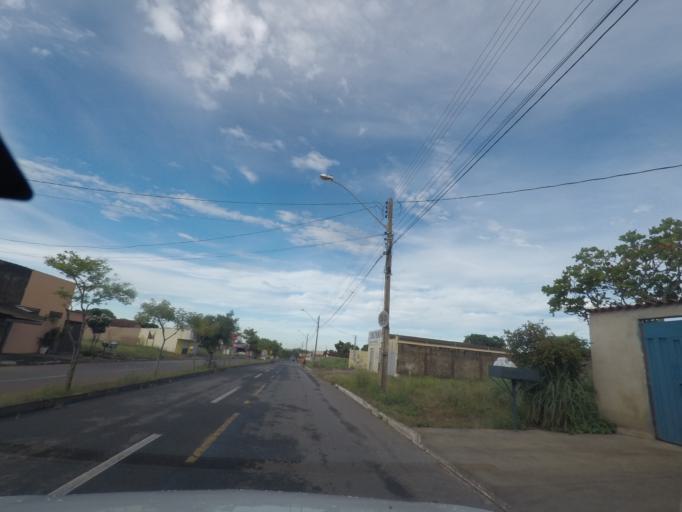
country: BR
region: Goias
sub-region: Aparecida De Goiania
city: Aparecida de Goiania
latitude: -16.7868
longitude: -49.3650
